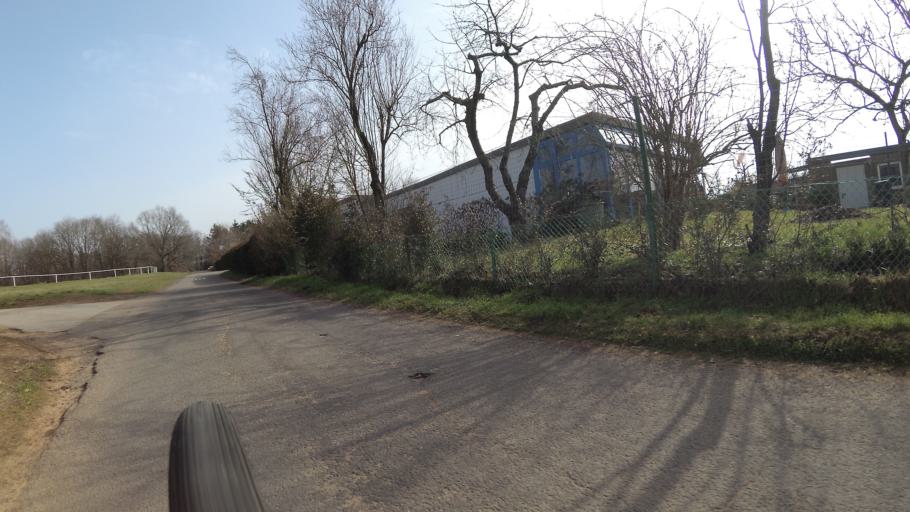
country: DE
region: Saarland
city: Nalbach
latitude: 49.4318
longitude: 6.7534
